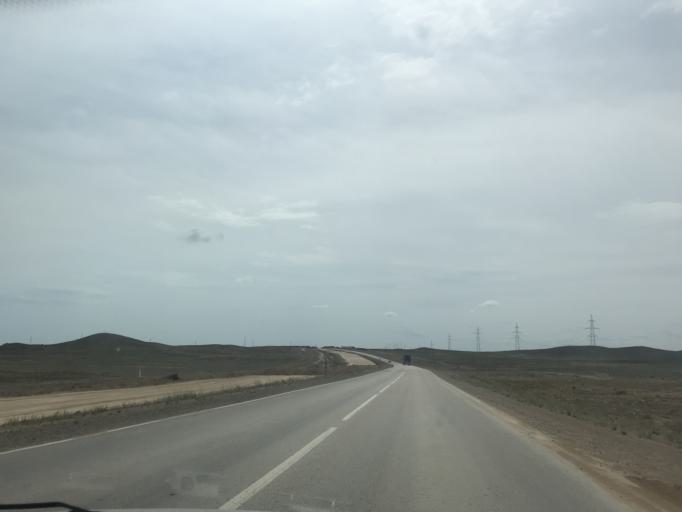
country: KZ
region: Zhambyl
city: Mynaral
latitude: 45.3499
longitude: 73.6888
